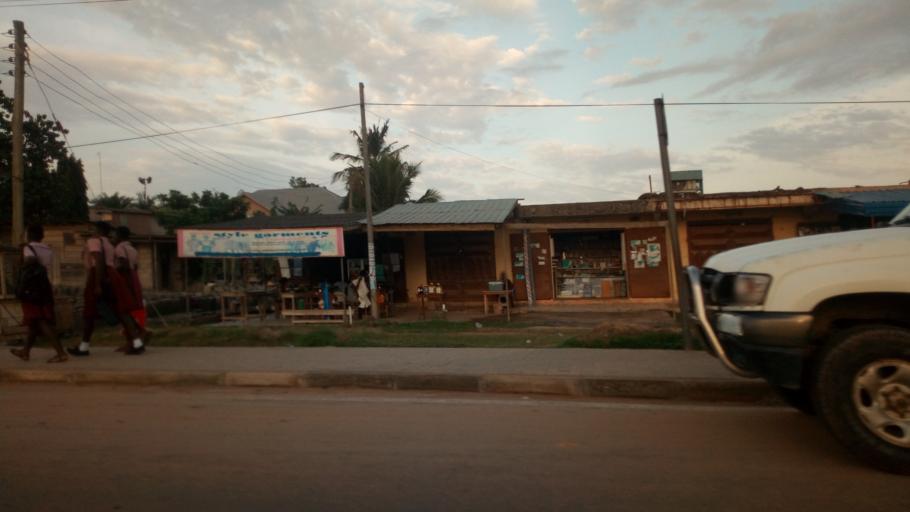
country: GH
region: Western
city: Takoradi
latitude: 4.9335
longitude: -1.7790
